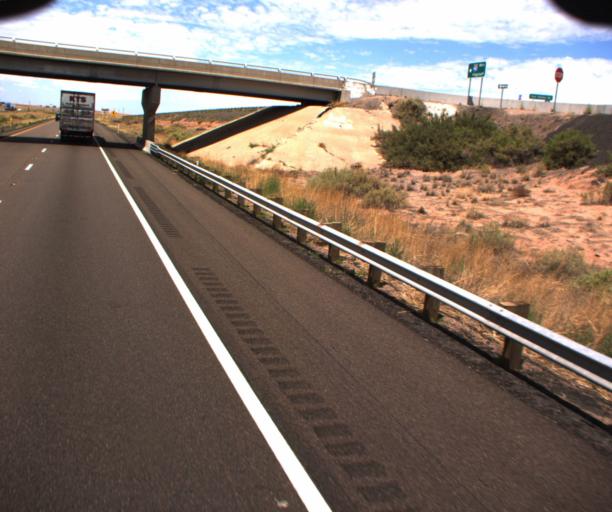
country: US
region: Arizona
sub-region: Navajo County
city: Holbrook
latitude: 34.9804
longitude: -110.0574
